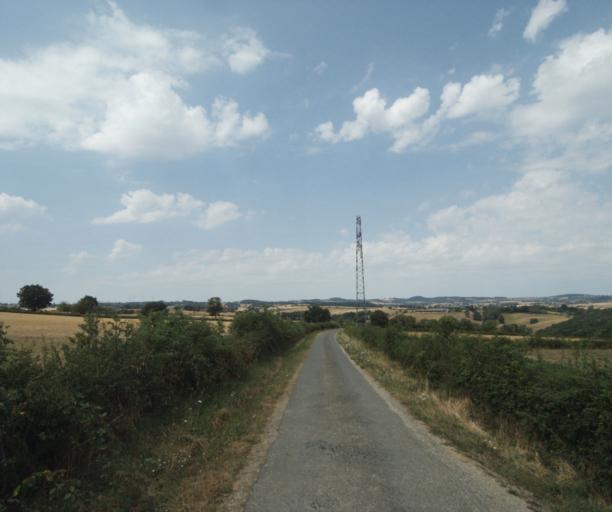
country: FR
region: Bourgogne
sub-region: Departement de Saone-et-Loire
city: Gueugnon
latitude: 46.6096
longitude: 4.0140
